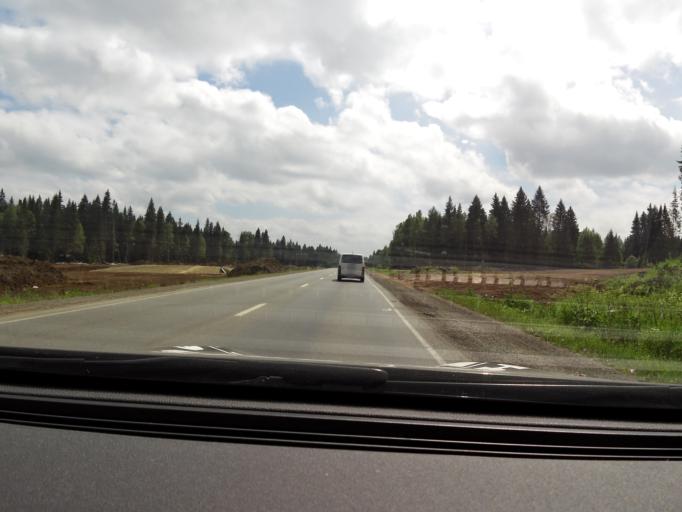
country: RU
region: Perm
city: Bershet'
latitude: 57.7021
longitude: 56.3839
